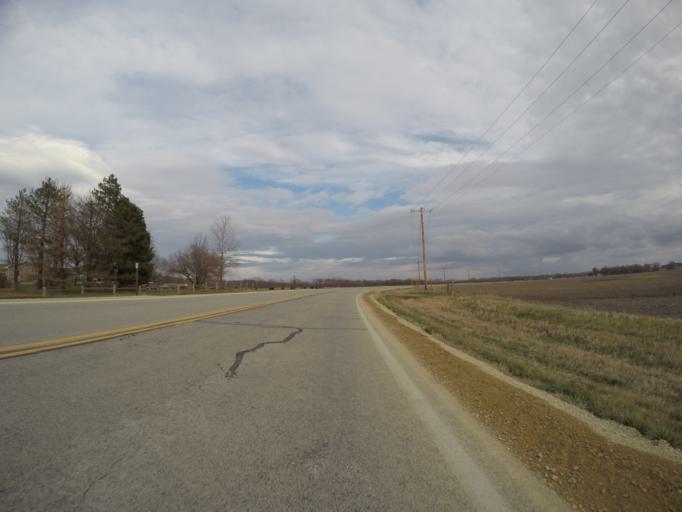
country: US
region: Kansas
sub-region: Riley County
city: Manhattan
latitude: 39.2260
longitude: -96.5593
